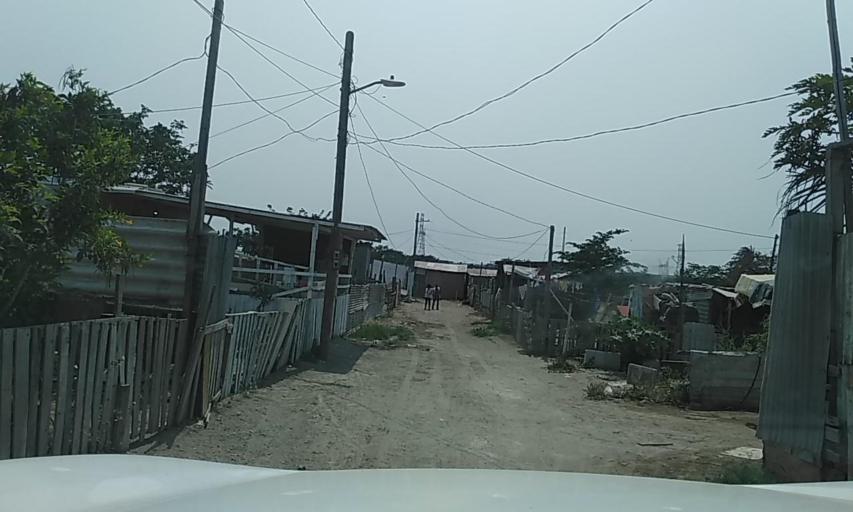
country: MX
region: Veracruz
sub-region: Veracruz
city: Las Amapolas
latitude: 19.1773
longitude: -96.1783
